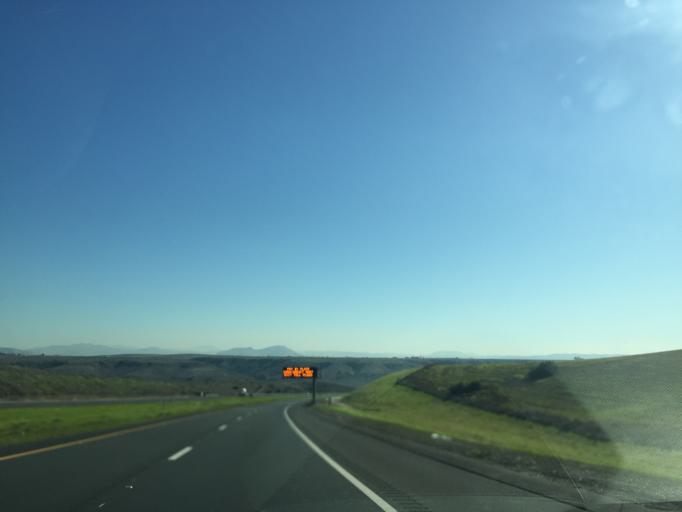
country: US
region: California
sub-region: San Diego County
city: Bonita
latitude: 32.6059
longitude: -116.9660
